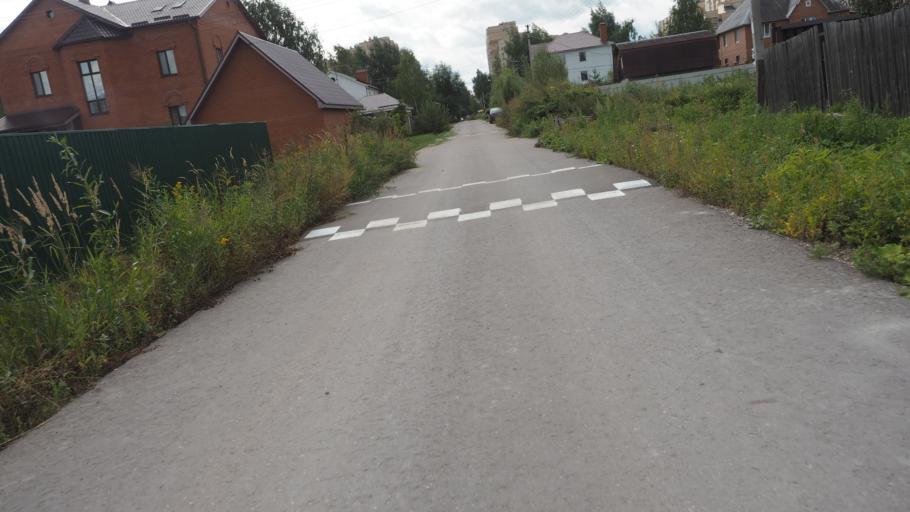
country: RU
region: Moskovskaya
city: Ramenskoye
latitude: 55.5780
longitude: 38.2589
